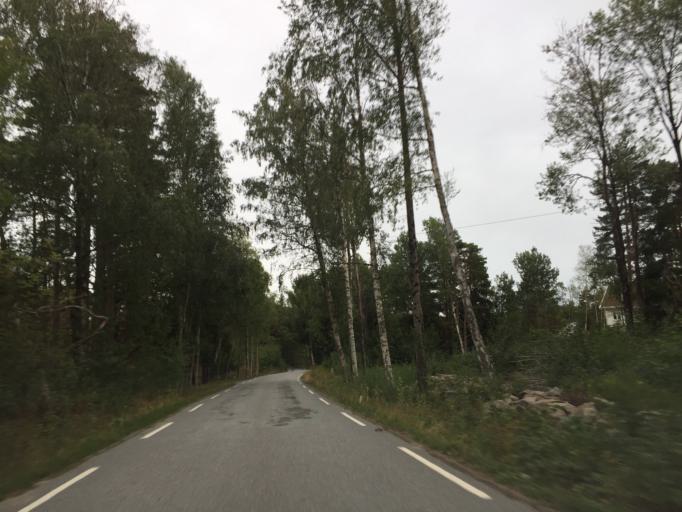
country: NO
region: Ostfold
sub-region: Hvaler
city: Skjaerhalden
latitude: 59.0612
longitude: 11.0075
